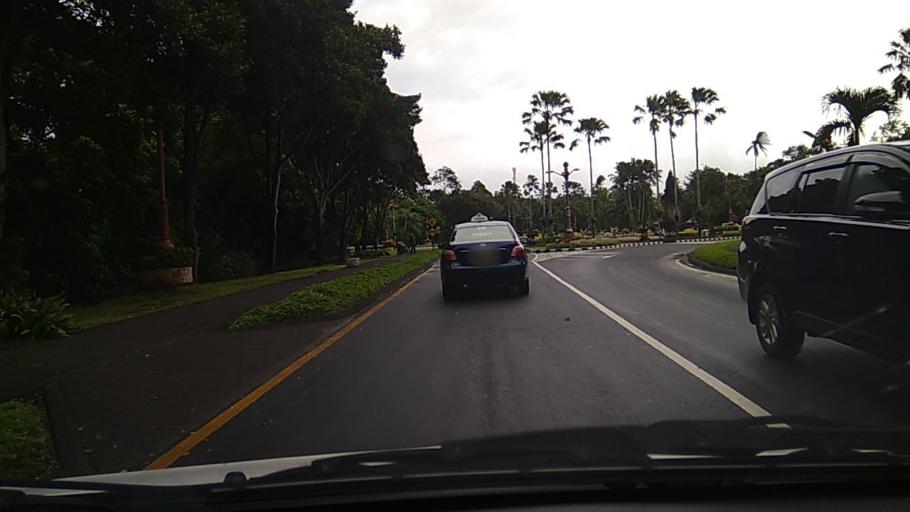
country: ID
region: Bali
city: Bualu
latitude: -8.7974
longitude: 115.2282
